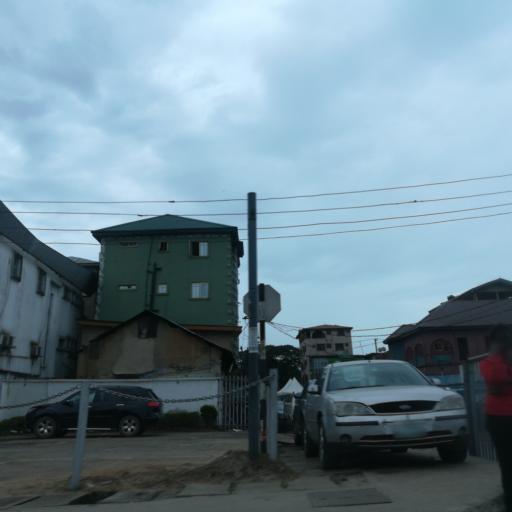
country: NG
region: Lagos
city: Ebute Metta
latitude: 6.4886
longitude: 3.3804
